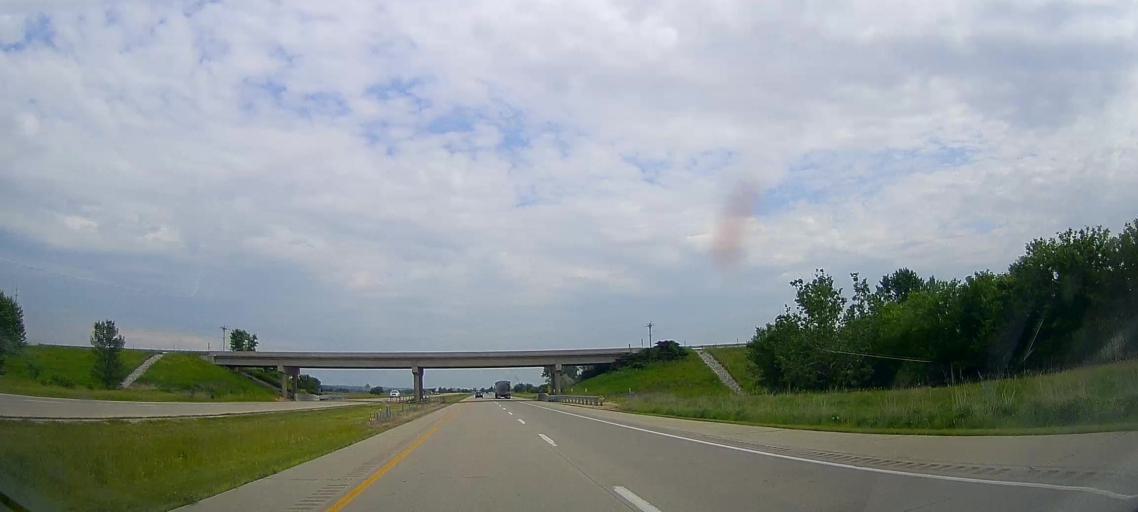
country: US
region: Nebraska
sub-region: Burt County
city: Tekamah
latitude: 41.8024
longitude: -96.0560
